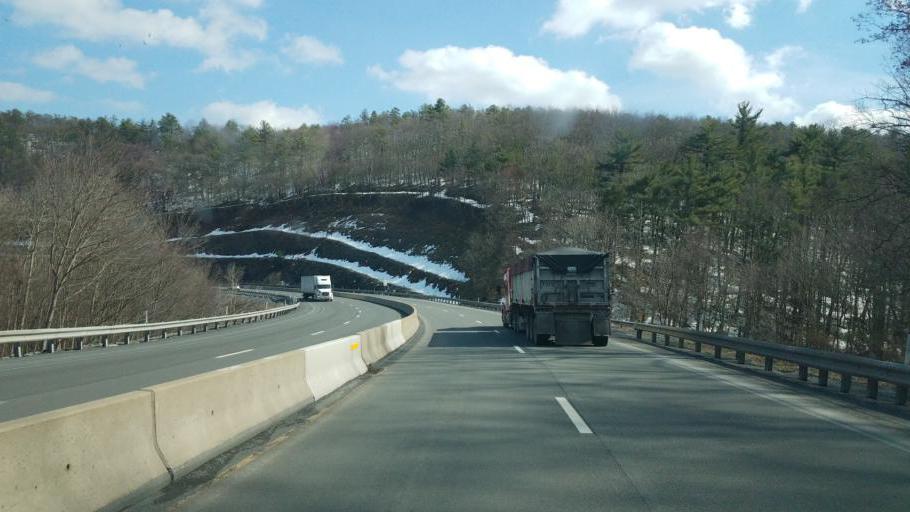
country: US
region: Pennsylvania
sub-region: Mifflin County
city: Milroy
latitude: 40.7277
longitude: -77.6288
